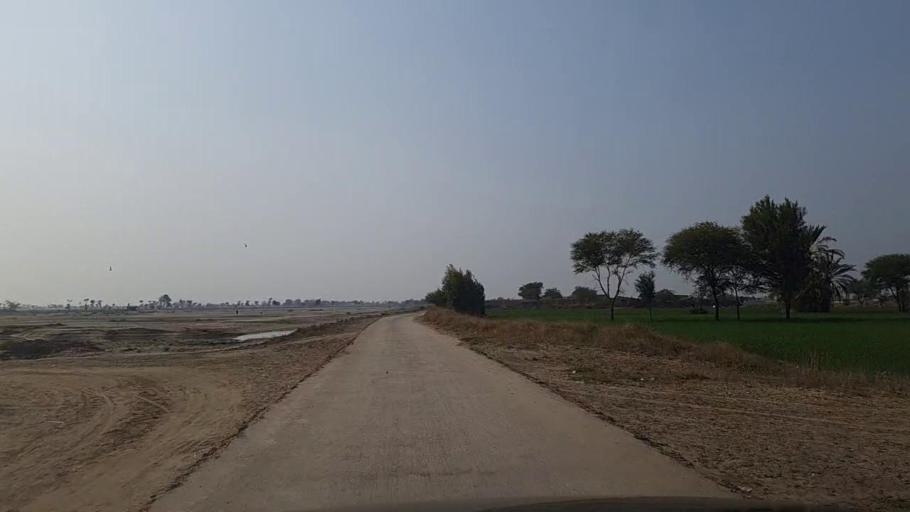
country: PK
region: Sindh
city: Daur
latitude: 26.3858
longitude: 68.4091
